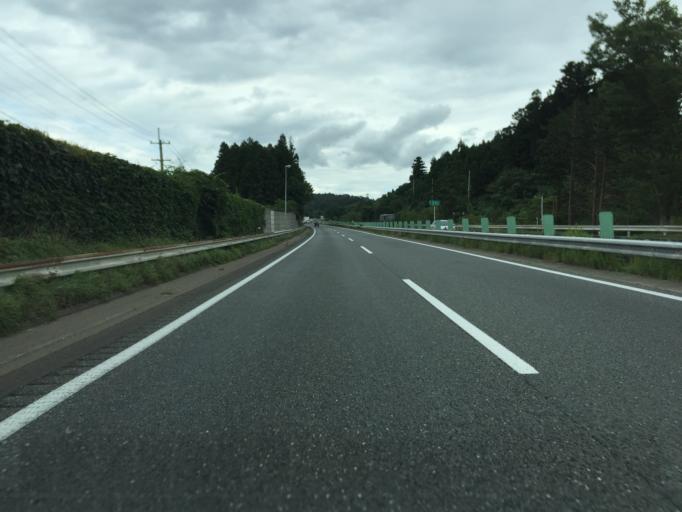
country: JP
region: Miyagi
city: Okawara
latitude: 38.1112
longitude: 140.6961
